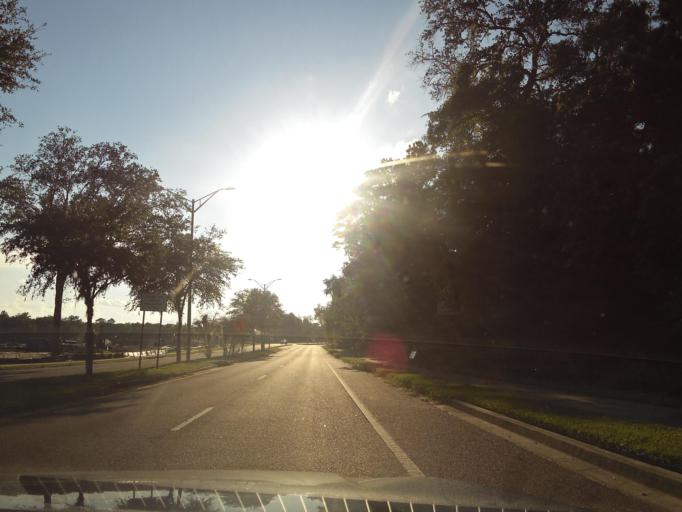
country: US
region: Florida
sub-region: Duval County
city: Jacksonville
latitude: 30.2482
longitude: -81.5632
